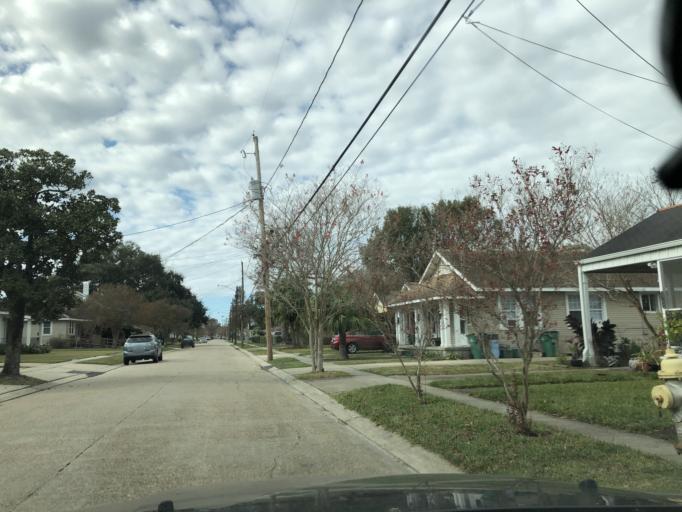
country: US
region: Louisiana
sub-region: Jefferson Parish
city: Metairie Terrace
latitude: 29.9760
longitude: -90.1643
